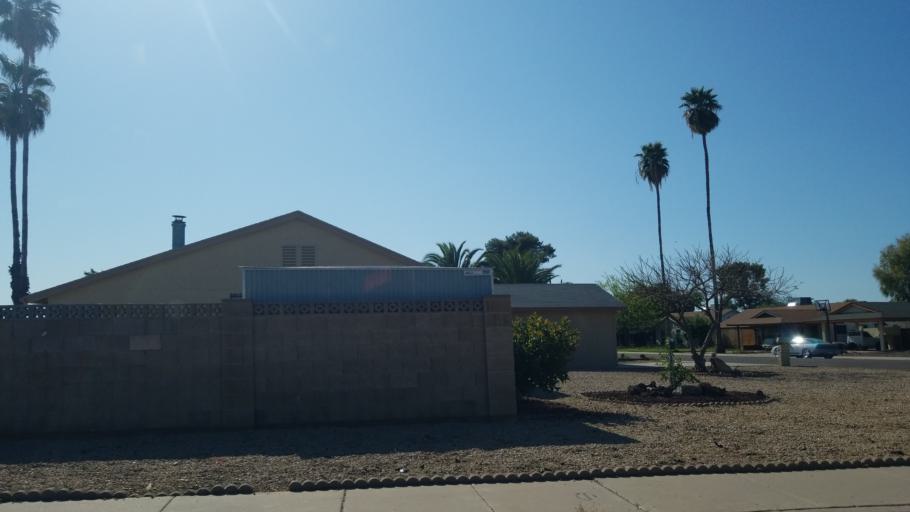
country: US
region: Arizona
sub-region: Maricopa County
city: Glendale
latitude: 33.5692
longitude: -112.1777
